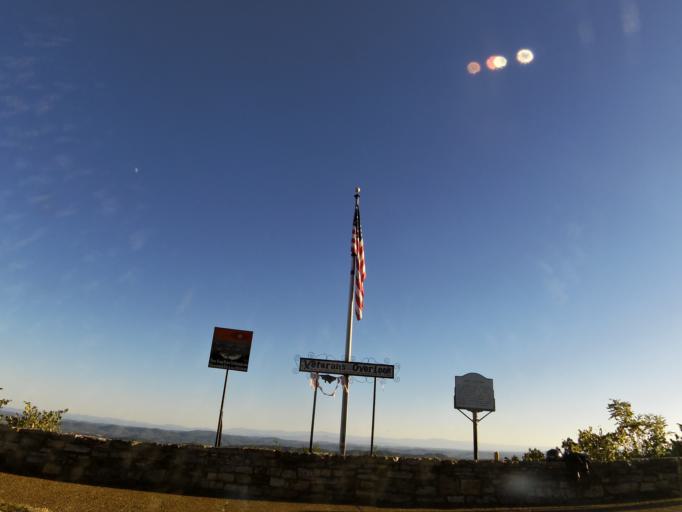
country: US
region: Tennessee
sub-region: Grainger County
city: Bean Station
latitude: 36.3497
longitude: -83.3938
